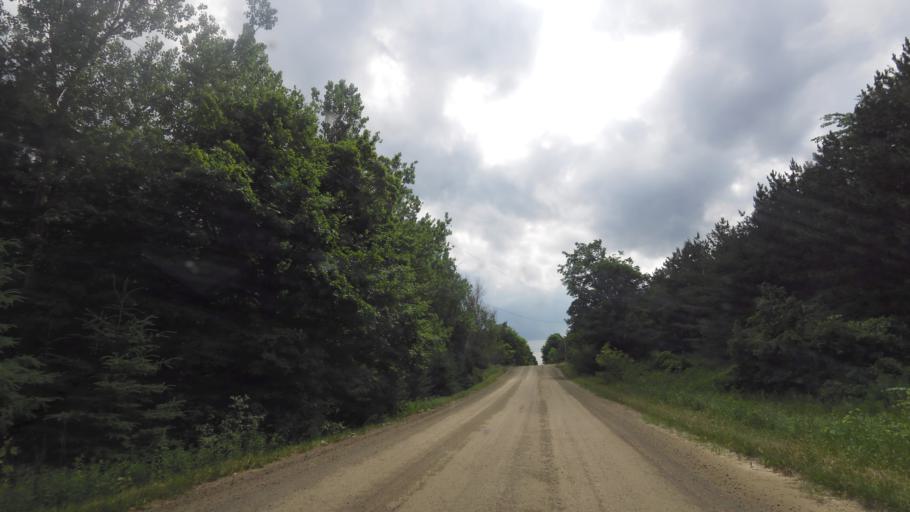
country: CA
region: Ontario
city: Orangeville
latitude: 43.8510
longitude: -79.9573
